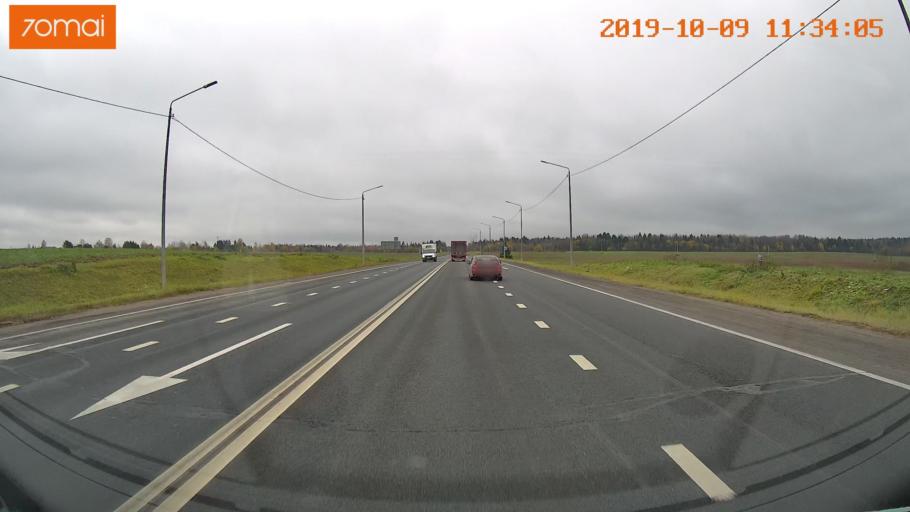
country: RU
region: Vologda
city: Gryazovets
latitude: 59.0194
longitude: 40.1165
